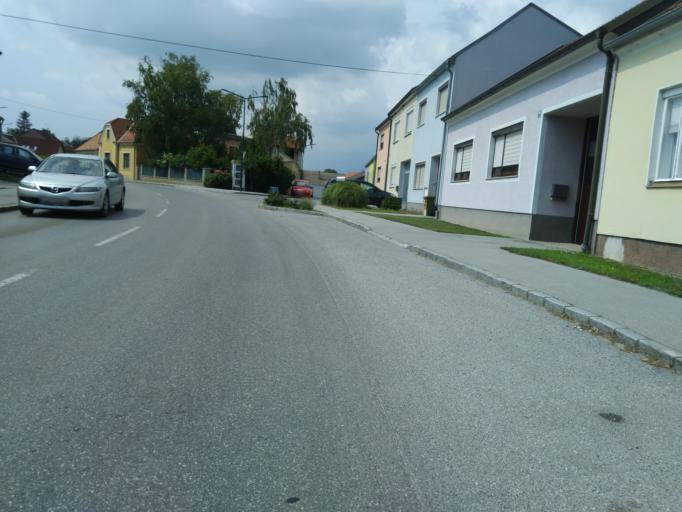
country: AT
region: Lower Austria
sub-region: Politischer Bezirk Ganserndorf
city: Ganserndorf
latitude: 48.3632
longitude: 16.7028
